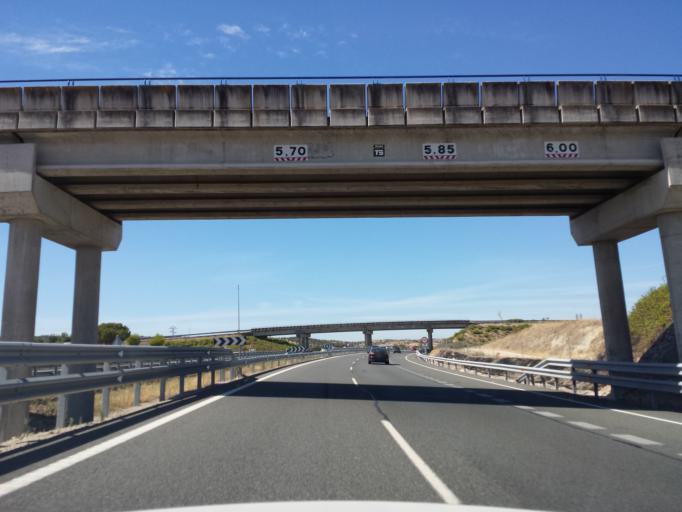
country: ES
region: Castille-La Mancha
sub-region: Province of Toledo
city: Lagartera
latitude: 39.9104
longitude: -5.2117
